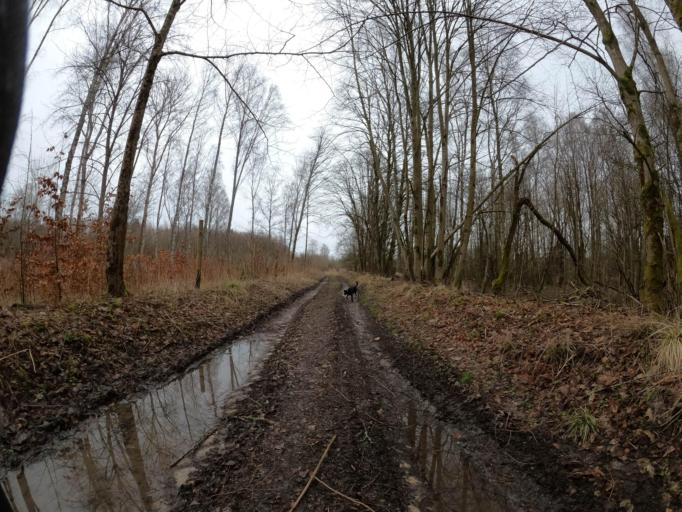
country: PL
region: Greater Poland Voivodeship
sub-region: Powiat zlotowski
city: Sypniewo
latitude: 53.4917
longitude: 16.5632
